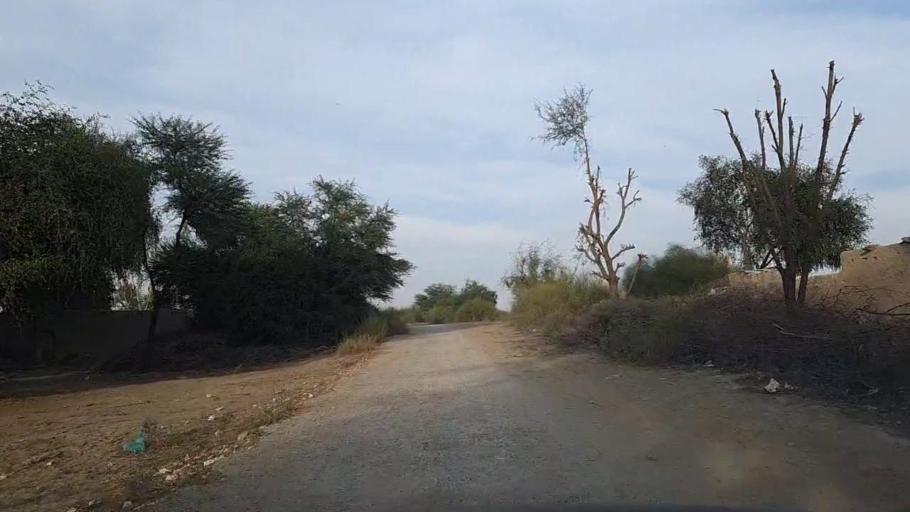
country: PK
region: Sindh
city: Jam Sahib
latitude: 26.4616
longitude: 68.5724
